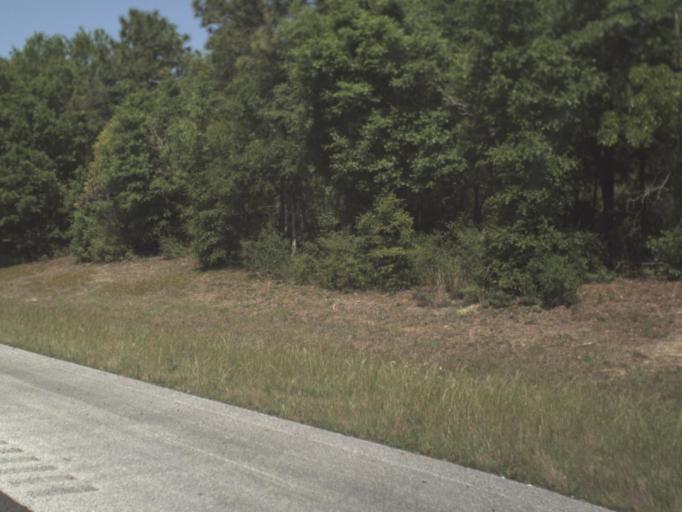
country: US
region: Florida
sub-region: Santa Rosa County
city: East Milton
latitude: 30.6247
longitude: -86.9458
